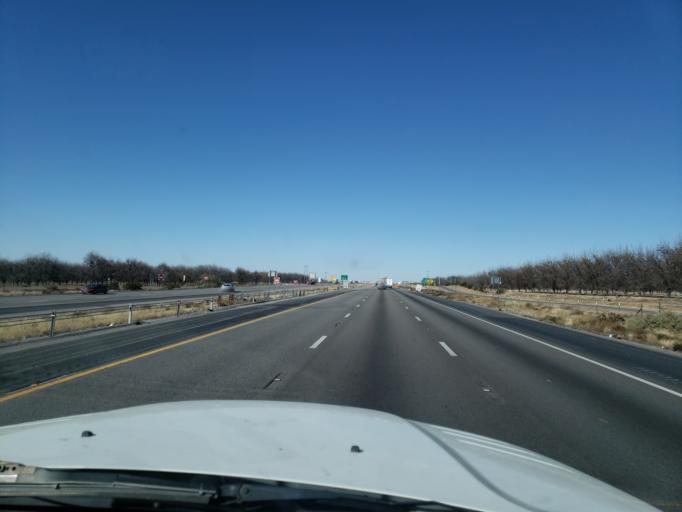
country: US
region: New Mexico
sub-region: Dona Ana County
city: University Park
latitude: 32.2385
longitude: -106.7160
